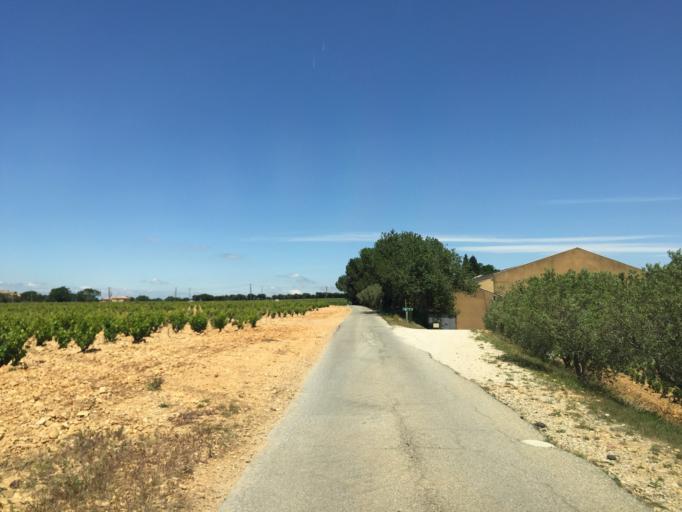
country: FR
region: Provence-Alpes-Cote d'Azur
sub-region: Departement du Vaucluse
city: Chateauneuf-du-Pape
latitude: 44.0518
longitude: 4.8499
